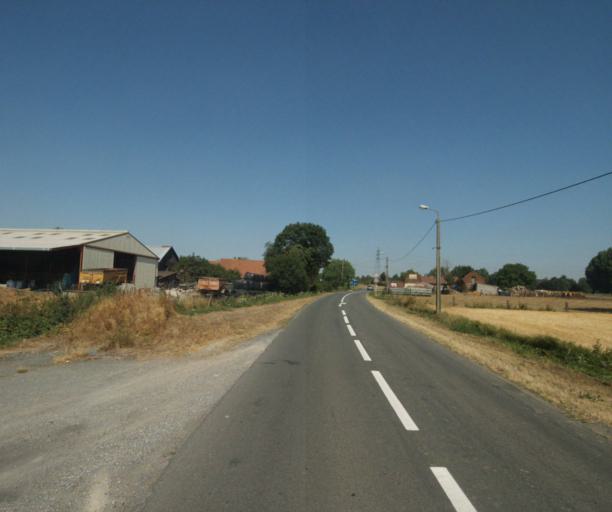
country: FR
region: Nord-Pas-de-Calais
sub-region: Departement du Nord
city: Wervicq-Sud
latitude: 50.7514
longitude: 3.0542
